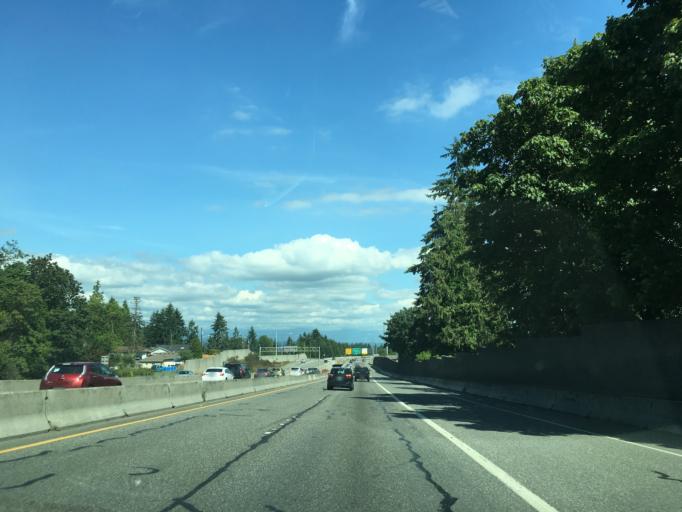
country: US
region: Washington
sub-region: Snohomish County
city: Everett
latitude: 47.9223
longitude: -122.2197
